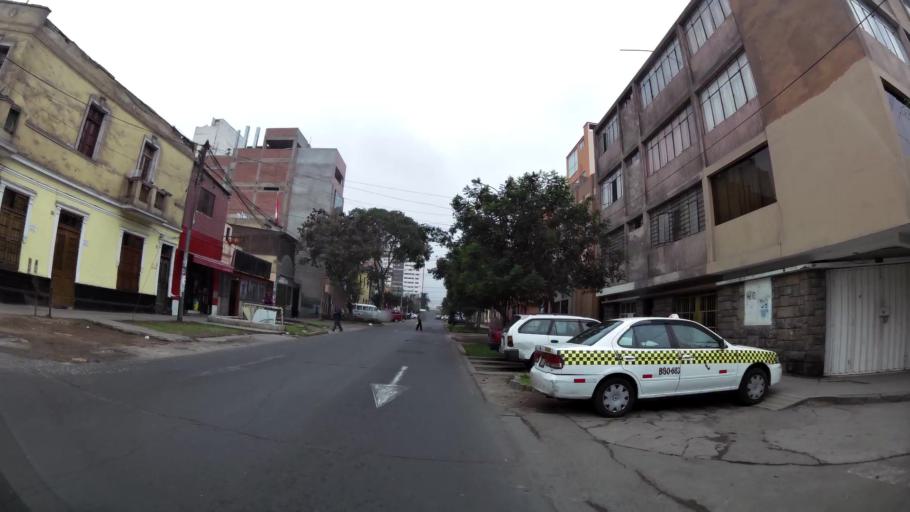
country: PE
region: Lima
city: Lima
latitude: -12.0773
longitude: -77.0328
